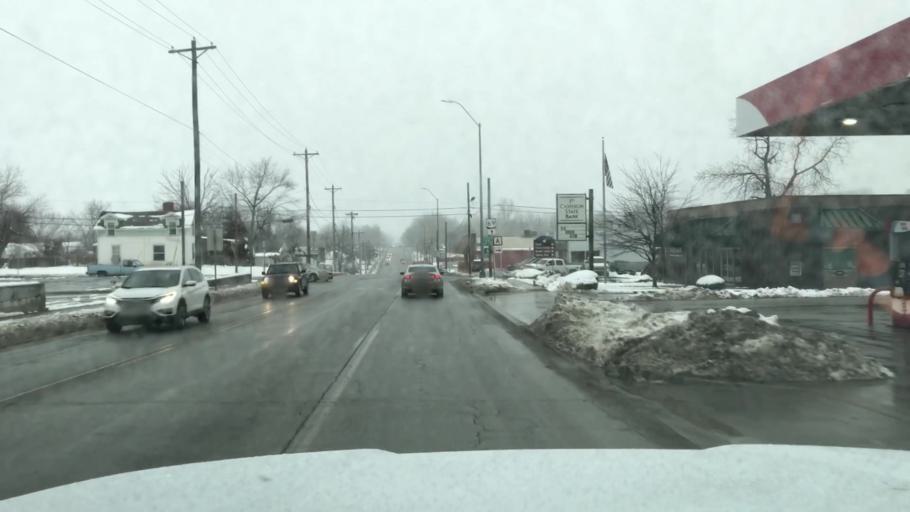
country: US
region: Missouri
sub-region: Clinton County
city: Cameron
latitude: 39.7396
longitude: -94.2360
